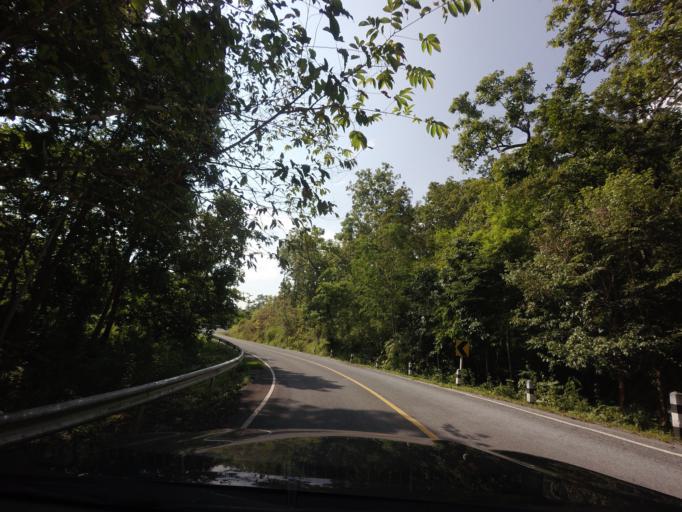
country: TH
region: Uttaradit
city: Ban Khok
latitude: 18.2489
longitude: 101.0005
